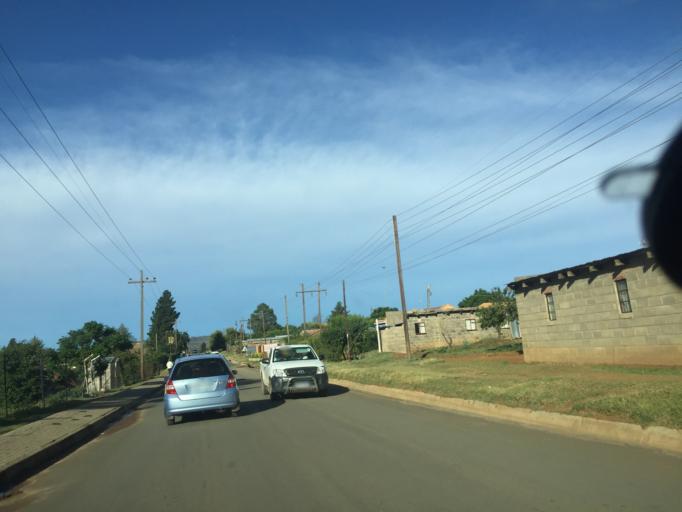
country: LS
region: Maseru
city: Maseru
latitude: -29.2891
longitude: 27.5309
